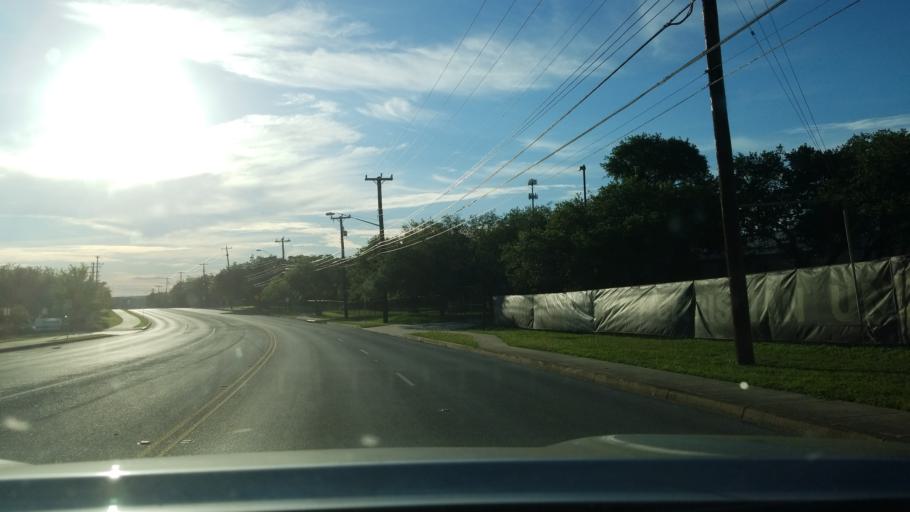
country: US
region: Texas
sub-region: Bexar County
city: Hollywood Park
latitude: 29.6196
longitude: -98.4583
